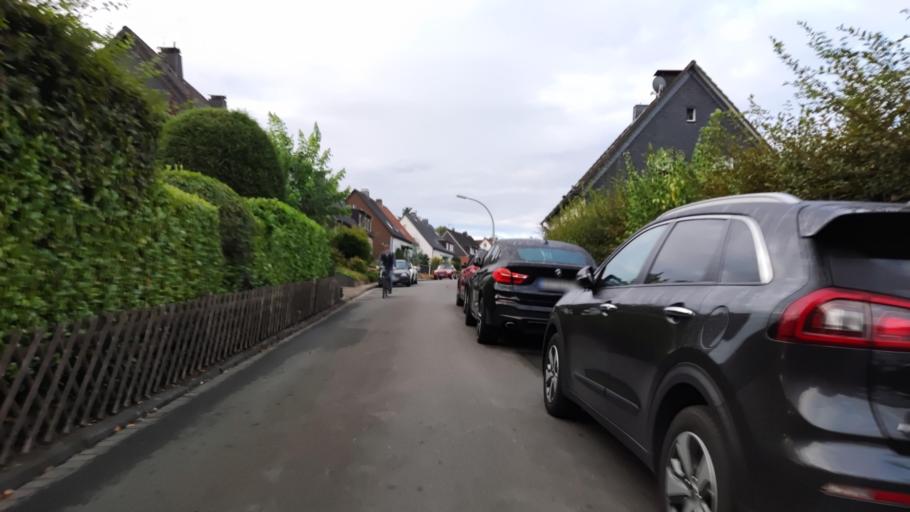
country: DE
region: North Rhine-Westphalia
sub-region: Regierungsbezirk Arnsberg
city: Herne
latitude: 51.5421
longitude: 7.2436
